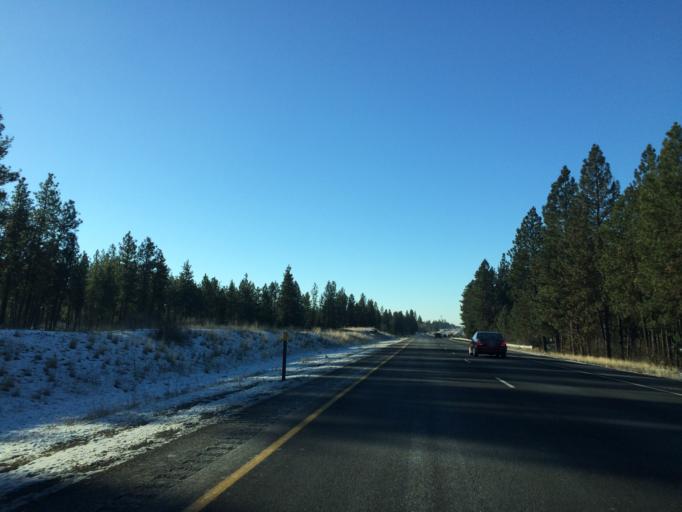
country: US
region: Washington
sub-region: Spokane County
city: Medical Lake
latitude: 47.5163
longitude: -117.6739
